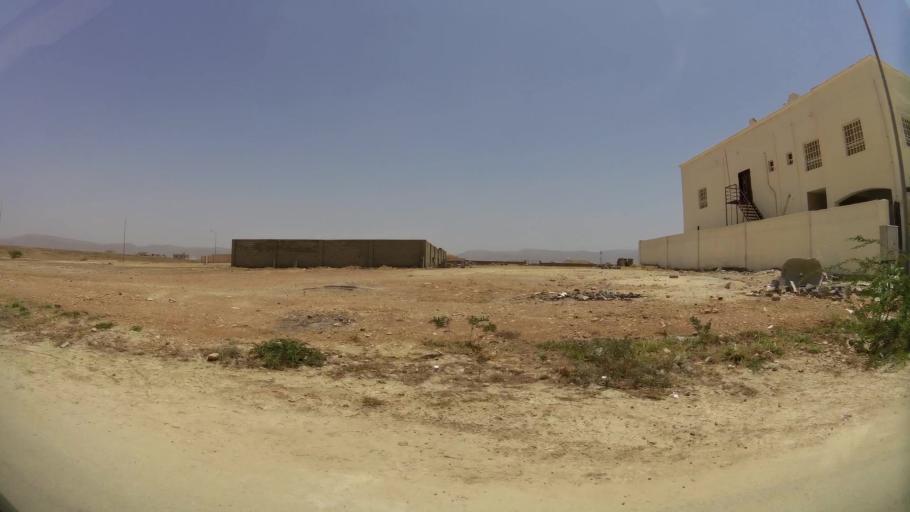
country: OM
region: Zufar
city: Salalah
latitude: 17.0865
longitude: 54.1823
